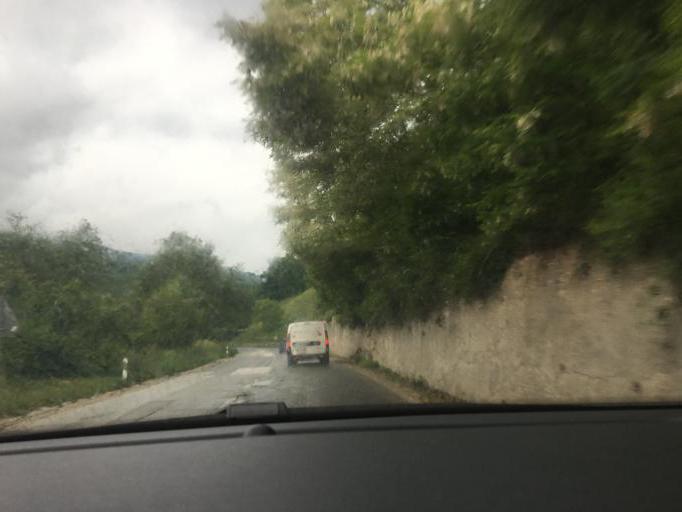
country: MK
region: Kicevo
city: Zajas
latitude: 41.6362
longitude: 20.9066
